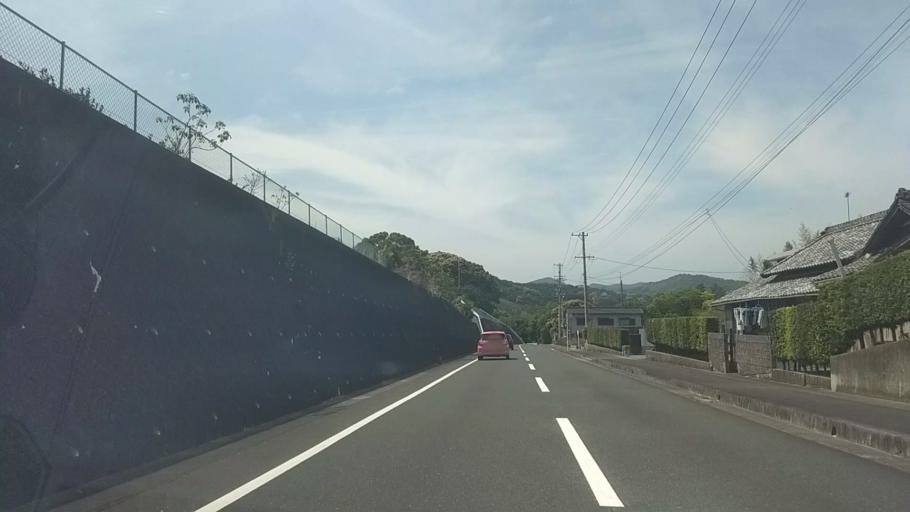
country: JP
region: Shizuoka
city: Kosai-shi
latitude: 34.7687
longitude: 137.5542
